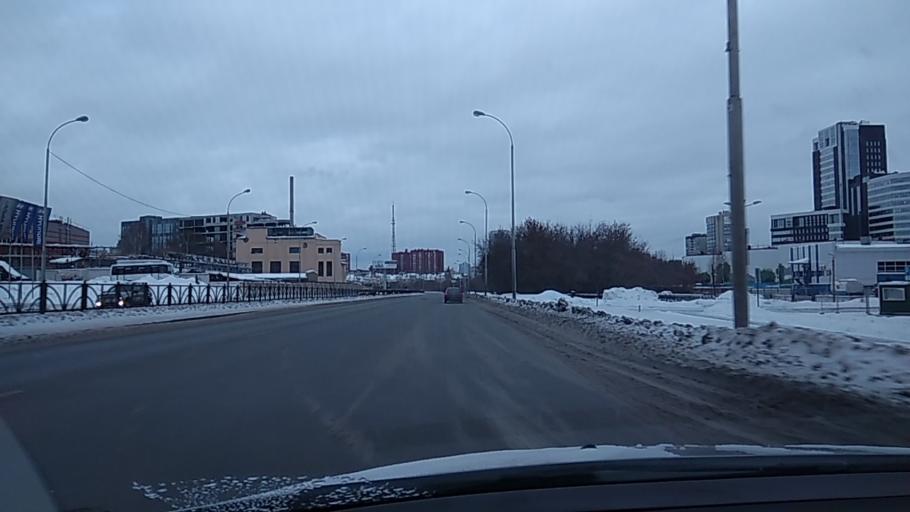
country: RU
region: Sverdlovsk
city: Yekaterinburg
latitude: 56.8132
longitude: 60.6291
